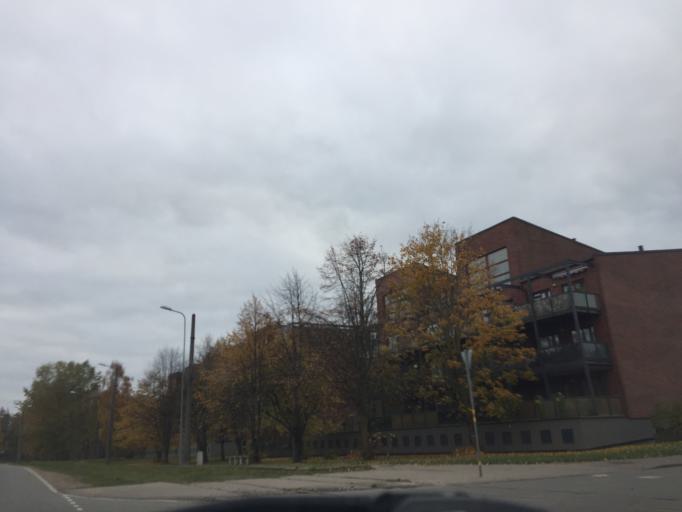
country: LV
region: Liepaja
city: Liepaja
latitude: 56.4861
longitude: 21.0058
